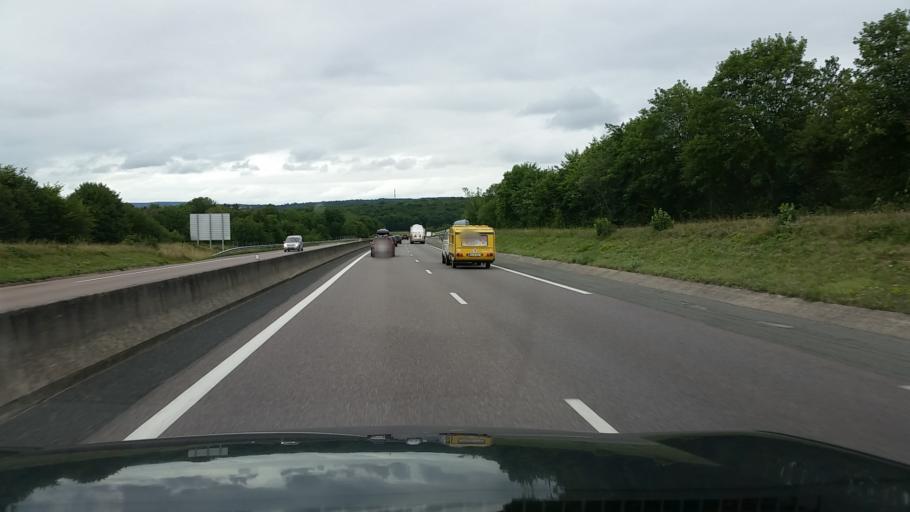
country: FR
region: Lorraine
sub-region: Departement de Meurthe-et-Moselle
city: Colombey-les-Belles
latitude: 48.4539
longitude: 5.8682
